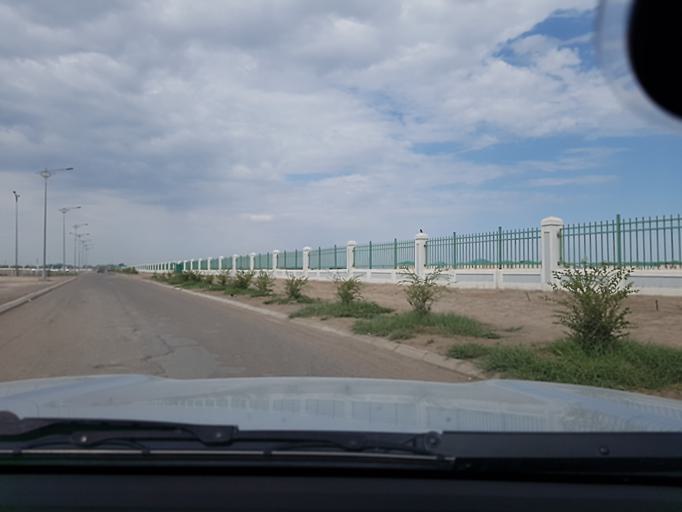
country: TM
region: Dasoguz
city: Dasoguz
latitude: 41.8813
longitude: 59.9500
